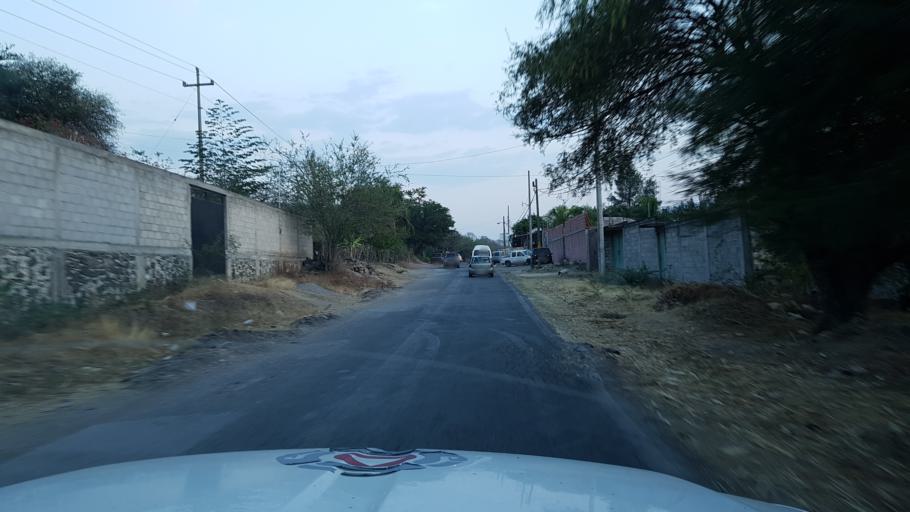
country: MX
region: Morelos
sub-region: Tlaltizapan de Zapata
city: Colonia Palo Prieto (Chipitongo)
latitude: 18.7066
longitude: -99.1067
